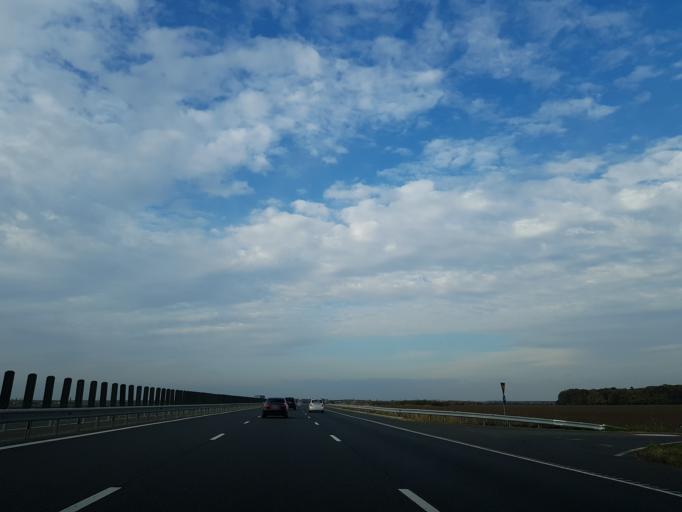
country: RO
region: Ilfov
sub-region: Comuna Moara Vlasiei
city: Caciulati
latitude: 44.5923
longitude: 26.1765
